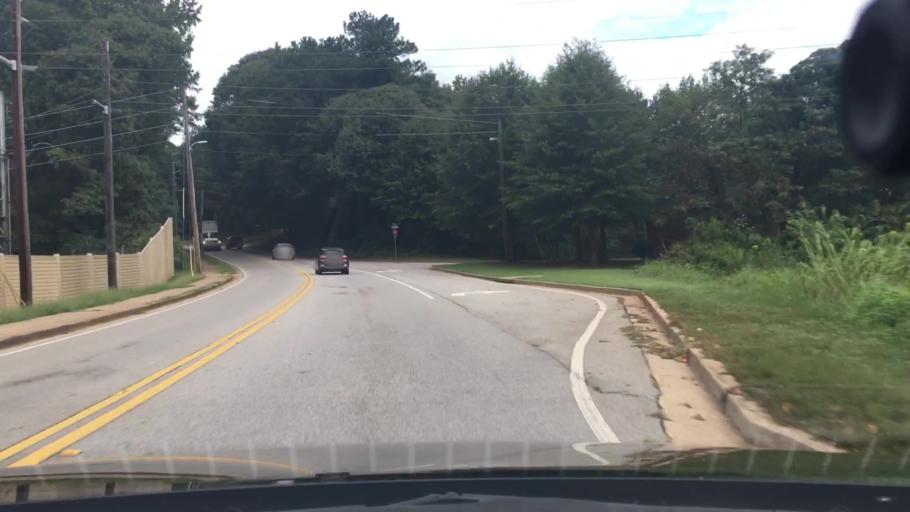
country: US
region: Georgia
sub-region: Coweta County
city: Newnan
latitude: 33.3729
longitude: -84.7859
